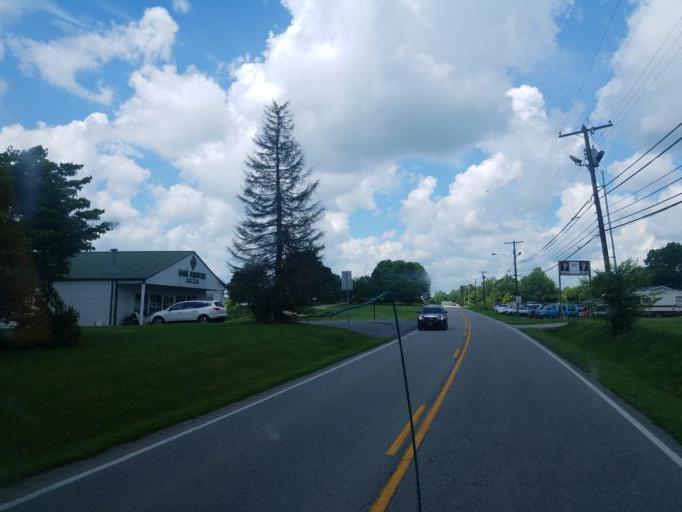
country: US
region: Kentucky
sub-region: Grayson County
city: Leitchfield
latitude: 37.4957
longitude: -86.2286
